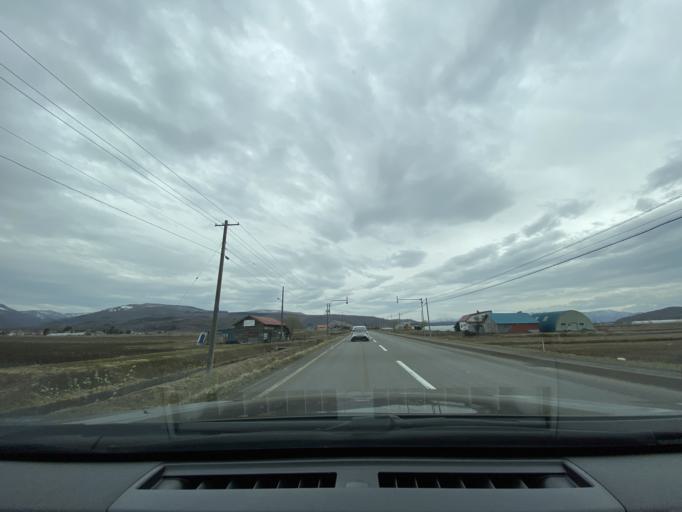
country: JP
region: Hokkaido
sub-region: Asahikawa-shi
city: Asahikawa
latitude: 43.8920
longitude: 142.5057
